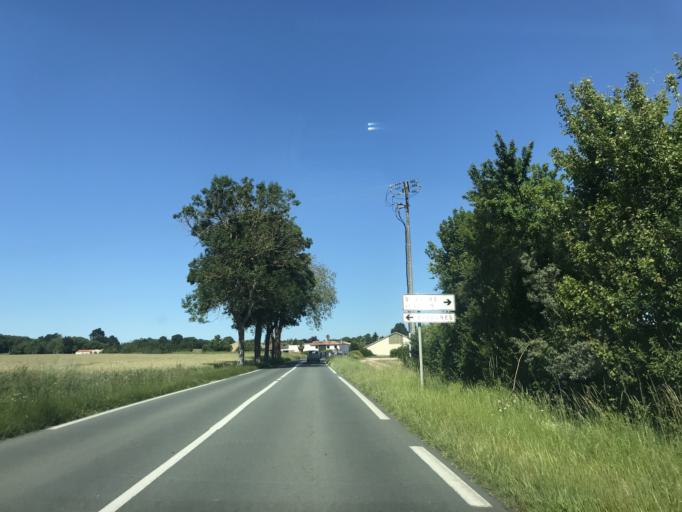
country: FR
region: Poitou-Charentes
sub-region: Departement de la Charente-Maritime
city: Cozes
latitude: 45.5758
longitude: -0.7682
